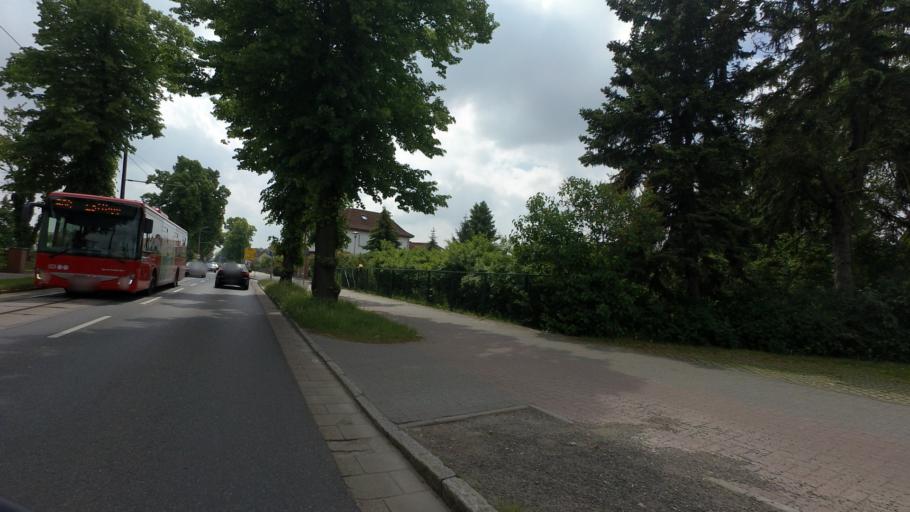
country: DE
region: Brandenburg
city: Cottbus
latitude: 51.7229
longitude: 14.3447
